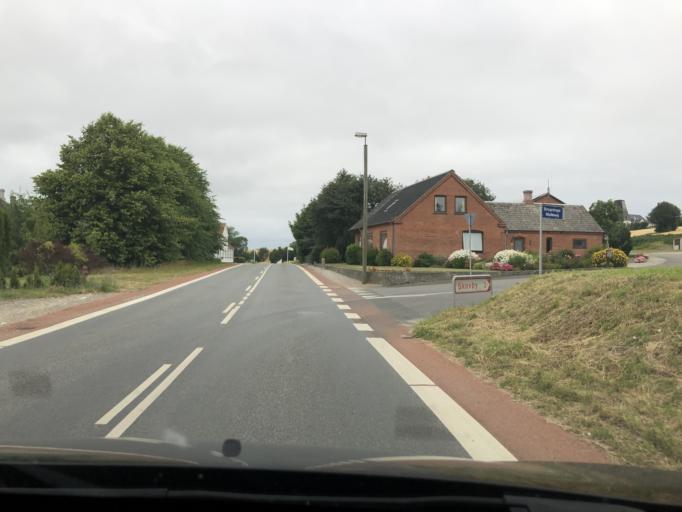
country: DK
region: South Denmark
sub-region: AEro Kommune
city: AEroskobing
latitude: 54.8977
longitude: 10.3072
